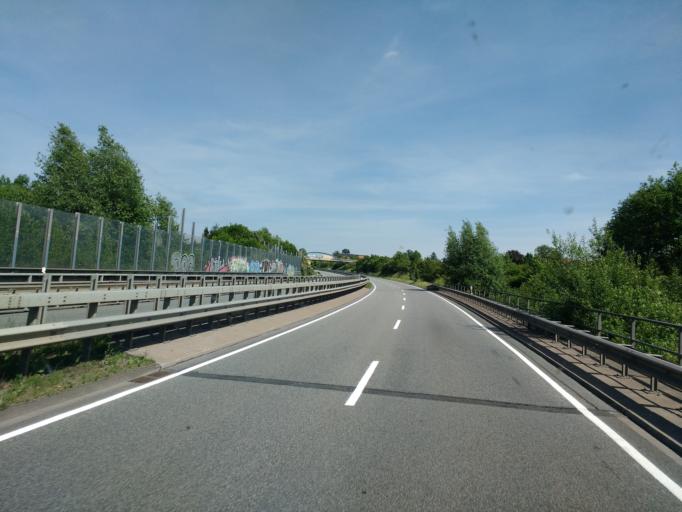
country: DE
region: North Rhine-Westphalia
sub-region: Regierungsbezirk Detmold
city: Herford
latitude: 52.0977
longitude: 8.6628
